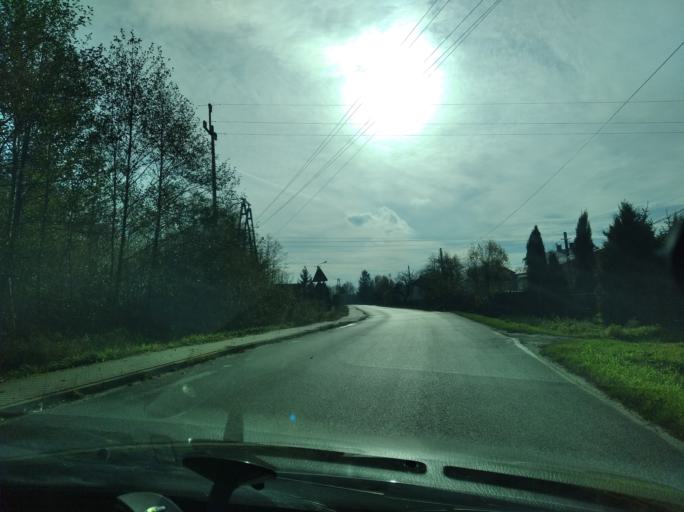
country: PL
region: Subcarpathian Voivodeship
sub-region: Powiat ropczycko-sedziszowski
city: Sedziszow Malopolski
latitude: 50.0844
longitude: 21.6982
